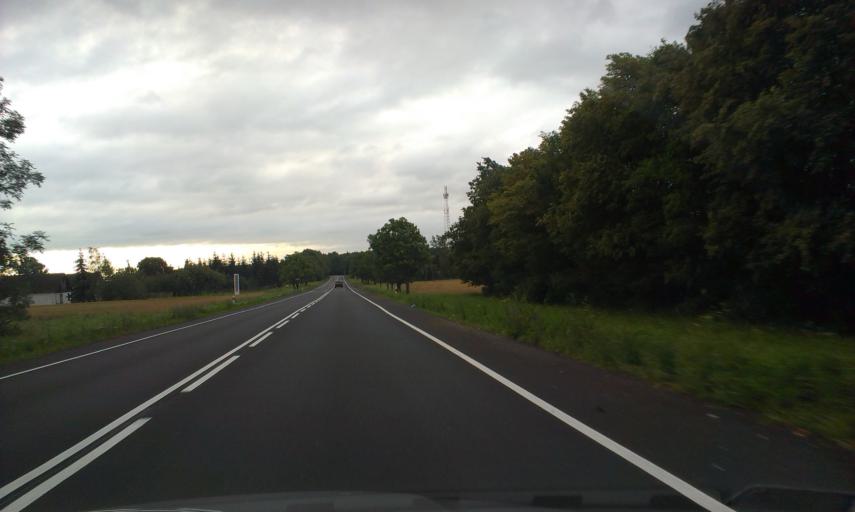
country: PL
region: Greater Poland Voivodeship
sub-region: Powiat pilski
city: Ujscie
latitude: 53.0346
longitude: 16.7780
